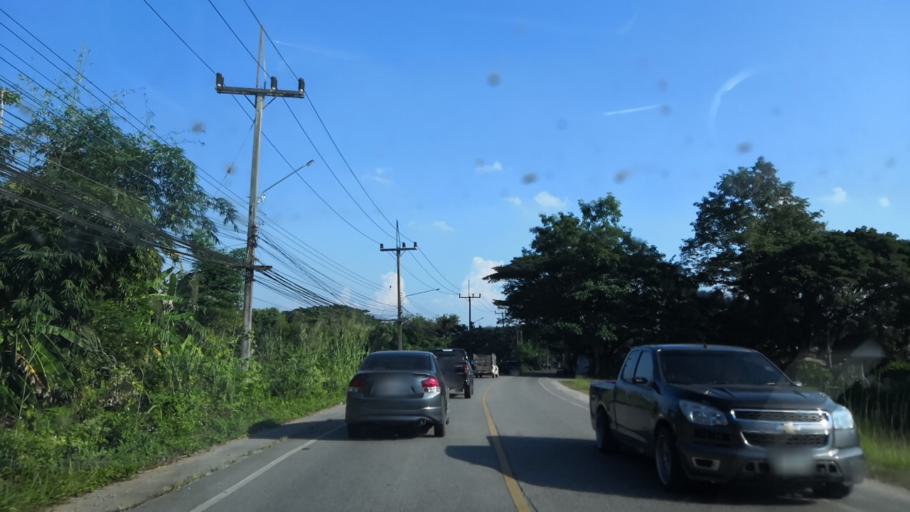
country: TH
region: Chiang Rai
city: Chiang Rai
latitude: 19.9310
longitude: 99.8671
